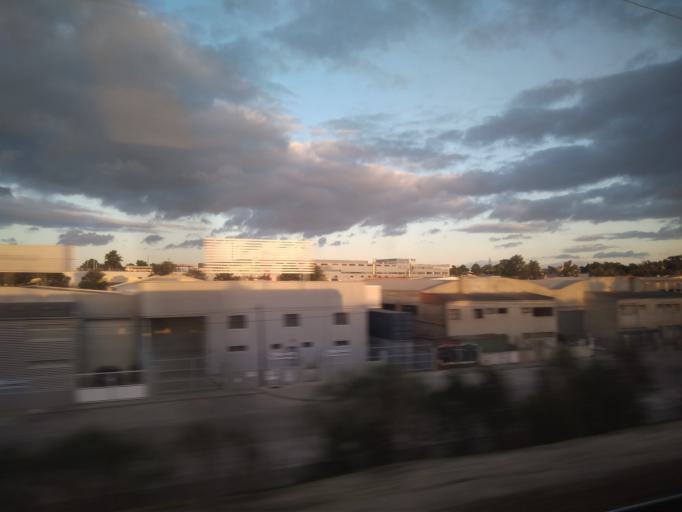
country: PT
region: Setubal
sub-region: Seixal
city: Corroios
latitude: 38.6299
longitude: -9.1422
